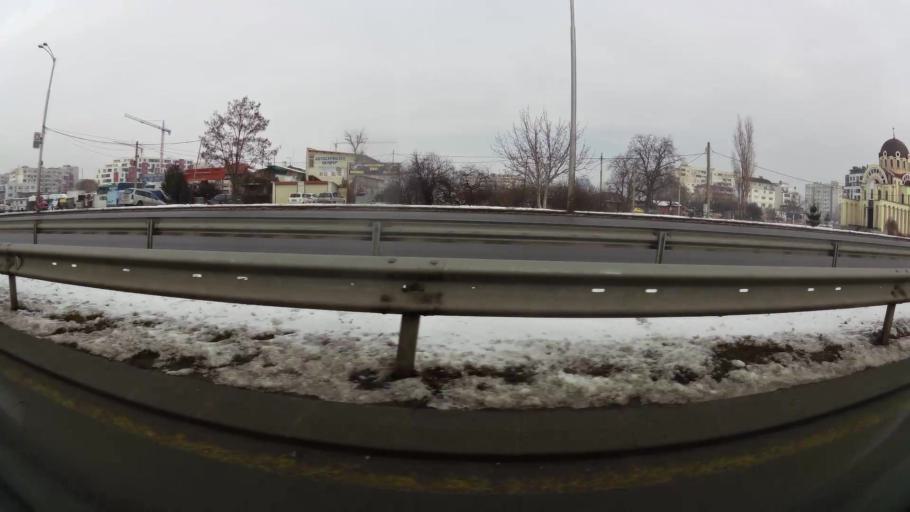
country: BG
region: Sofia-Capital
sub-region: Stolichna Obshtina
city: Sofia
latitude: 42.7108
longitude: 23.3830
